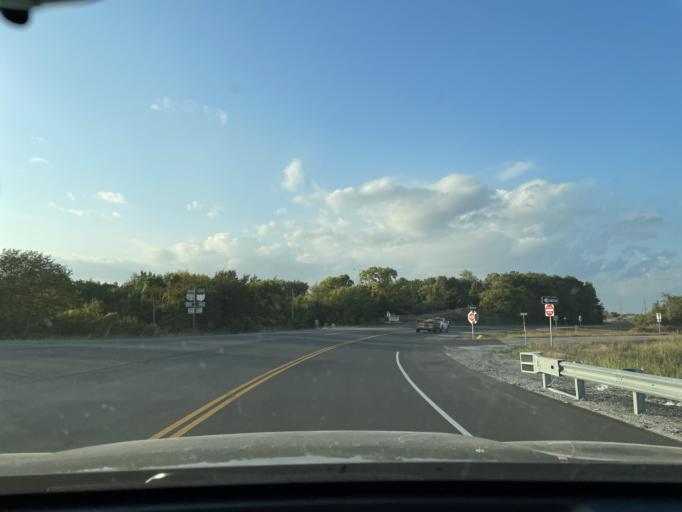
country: US
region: Missouri
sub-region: Andrew County
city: Country Club Village
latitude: 39.8360
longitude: -94.8656
